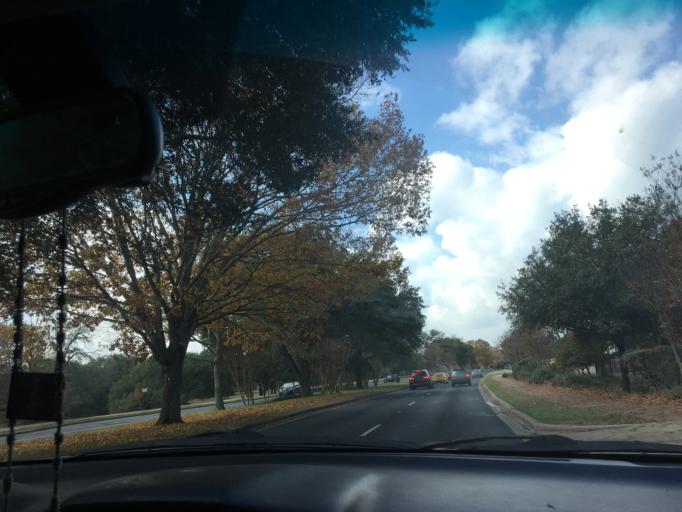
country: US
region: Texas
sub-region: Travis County
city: Shady Hollow
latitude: 30.2005
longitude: -97.8743
